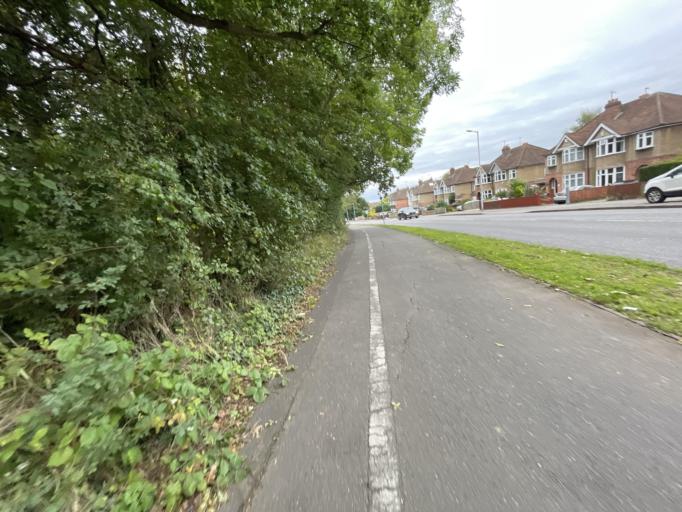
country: GB
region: England
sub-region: West Berkshire
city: Tilehurst
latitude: 51.4465
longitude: -1.0158
